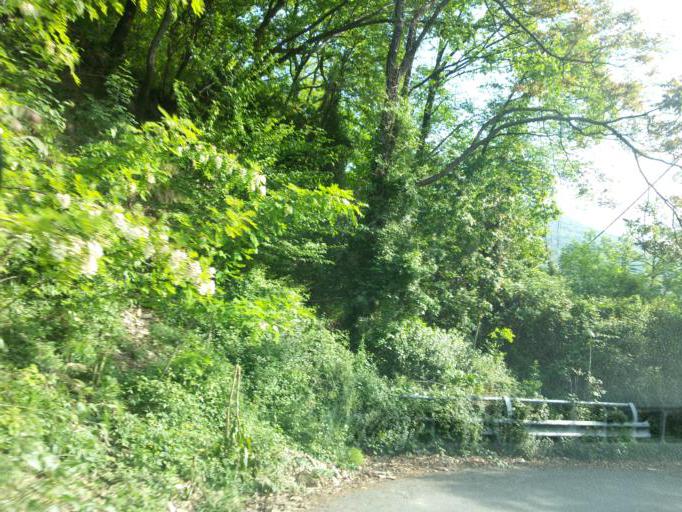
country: IT
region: Liguria
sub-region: Provincia di Genova
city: Piccarello
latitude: 44.4478
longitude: 8.9900
